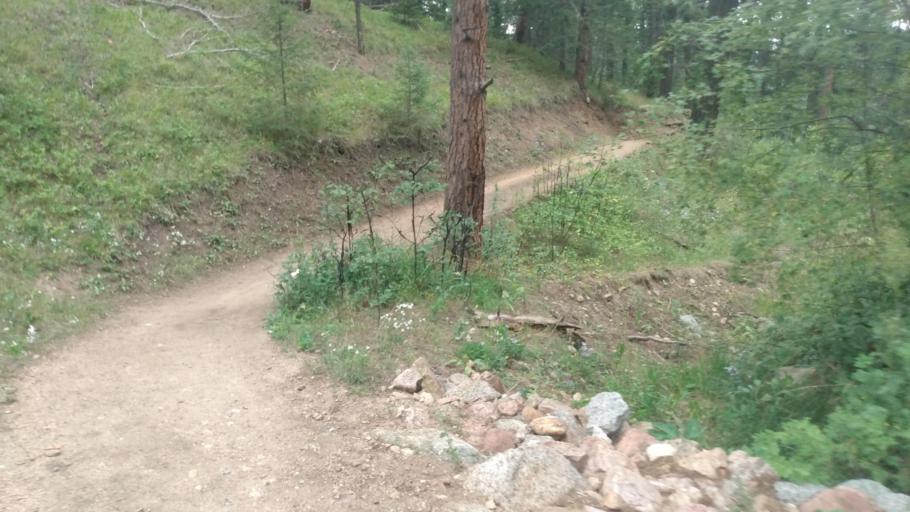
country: US
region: Colorado
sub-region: Boulder County
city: Boulder
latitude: 39.9944
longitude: -105.3080
